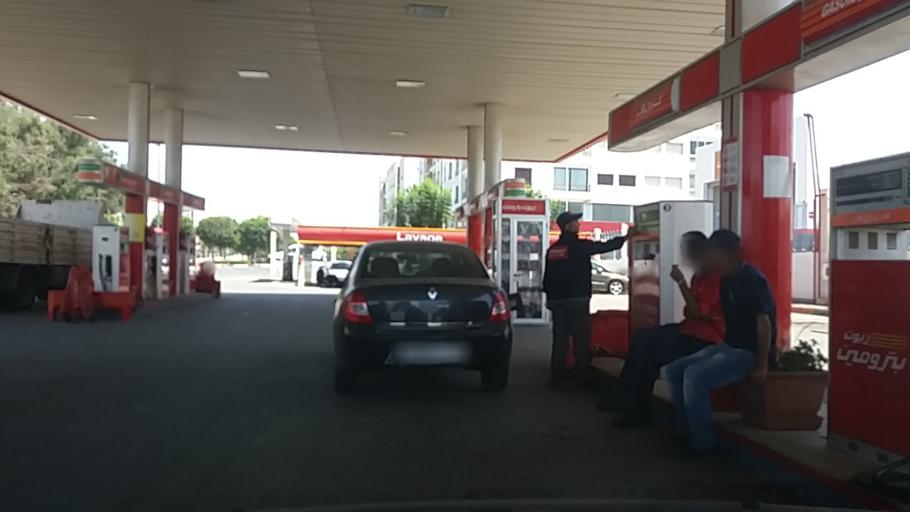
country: MA
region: Gharb-Chrarda-Beni Hssen
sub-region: Kenitra Province
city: Kenitra
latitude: 34.2486
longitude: -6.6086
